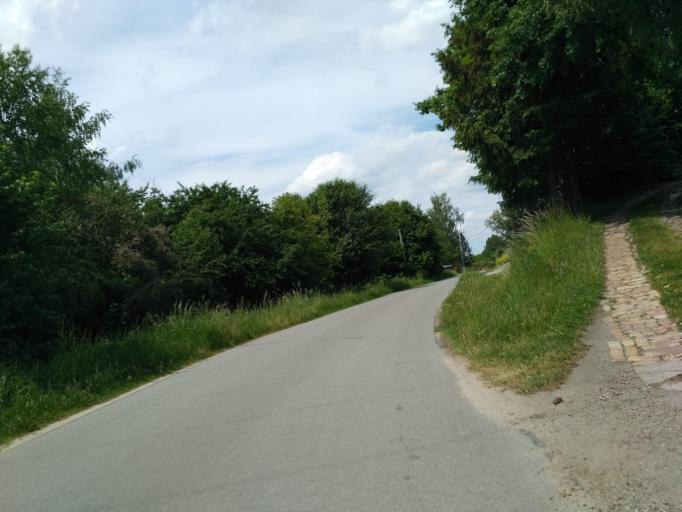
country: PL
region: Subcarpathian Voivodeship
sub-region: Powiat krosnienski
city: Odrzykon
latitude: 49.7130
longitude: 21.7452
